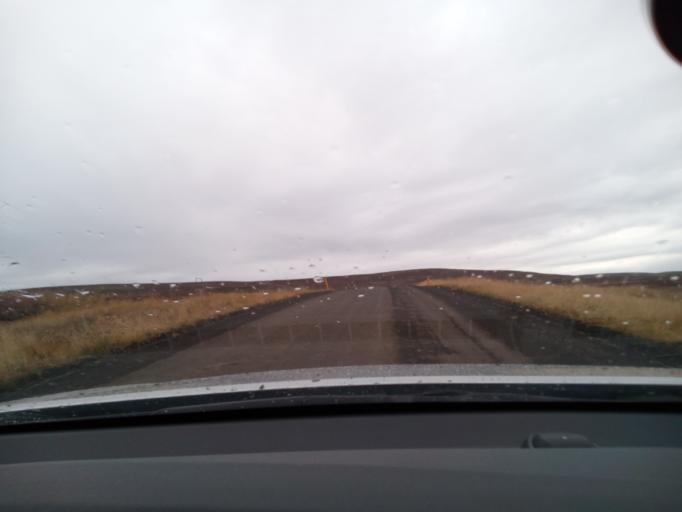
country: IS
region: Northeast
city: Laugar
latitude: 65.7887
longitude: -17.2266
